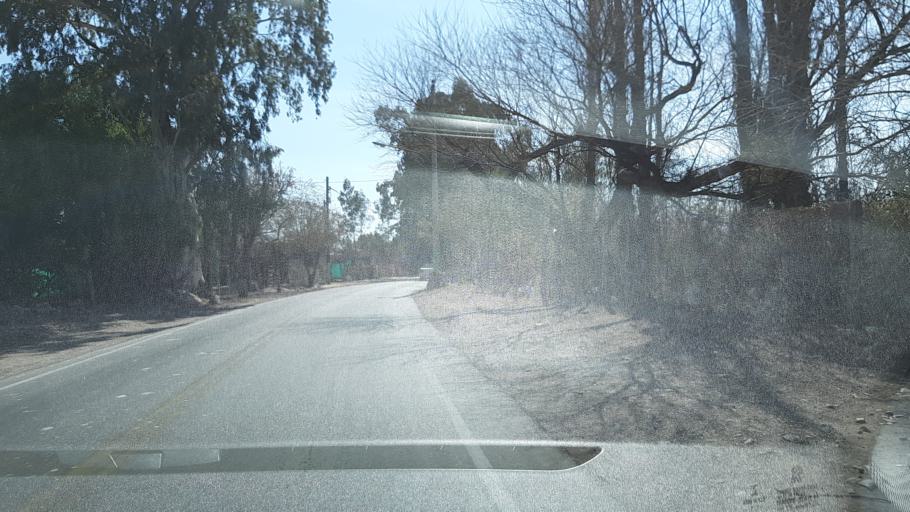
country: AR
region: San Juan
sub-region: Departamento de Rivadavia
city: Rivadavia
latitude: -31.5370
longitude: -68.6172
